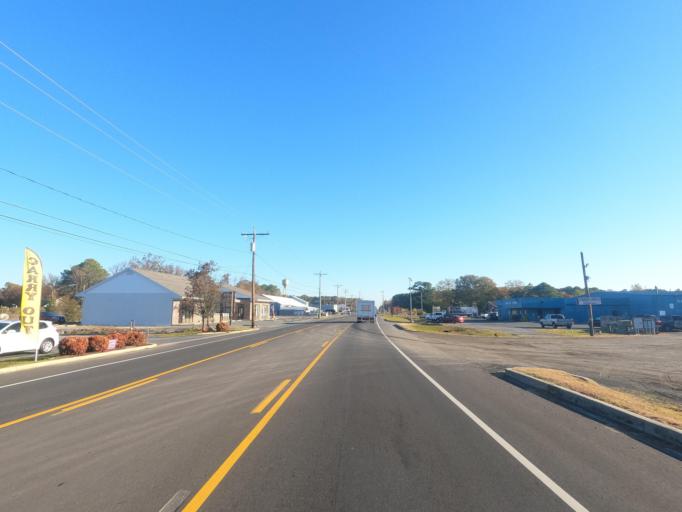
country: US
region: Maryland
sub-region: Somerset County
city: Crisfield
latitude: 37.9928
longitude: -75.8414
